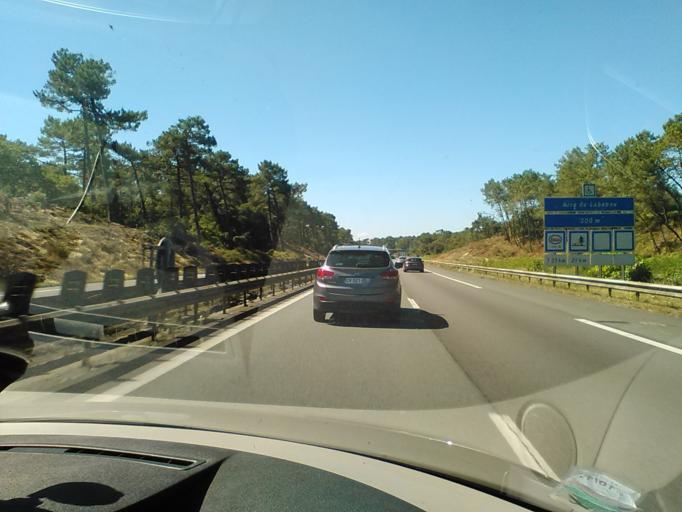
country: FR
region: Aquitaine
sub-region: Departement des Landes
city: Labenne
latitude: 43.5926
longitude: -1.4170
